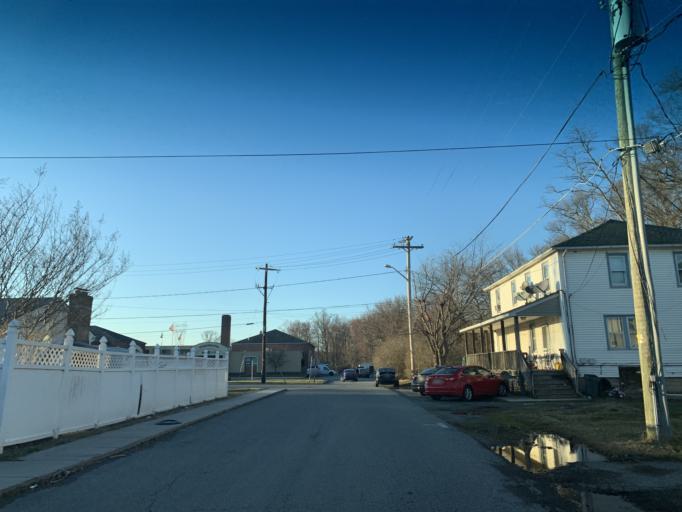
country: US
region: Maryland
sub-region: Cecil County
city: Perryville
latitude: 39.5613
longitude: -76.0753
